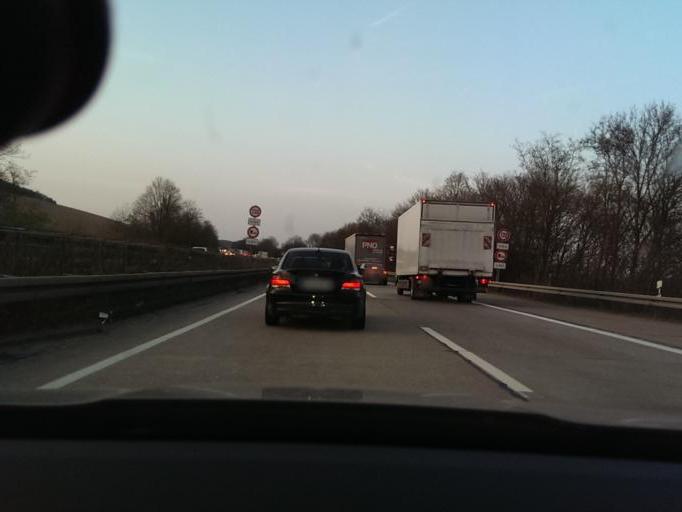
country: DE
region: Lower Saxony
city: Northeim
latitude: 51.7446
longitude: 10.0074
